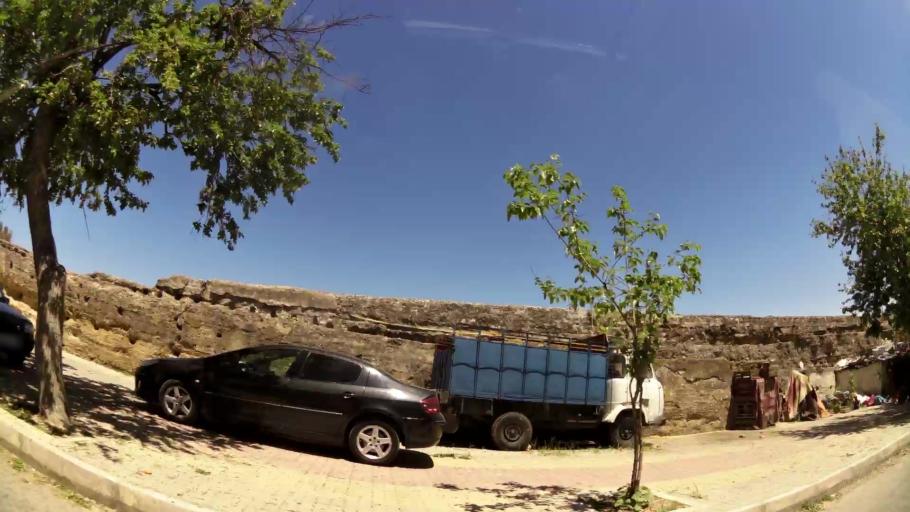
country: MA
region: Meknes-Tafilalet
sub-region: Meknes
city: Meknes
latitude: 33.9095
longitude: -5.5764
